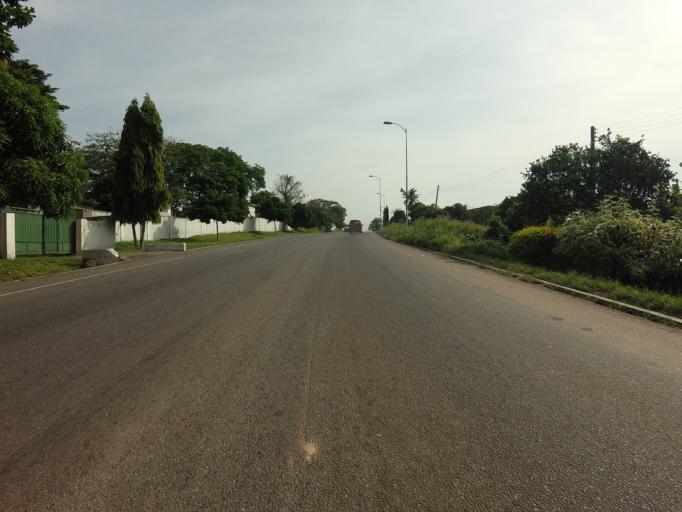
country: GH
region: Eastern
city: Aburi
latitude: 5.8350
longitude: -0.1810
